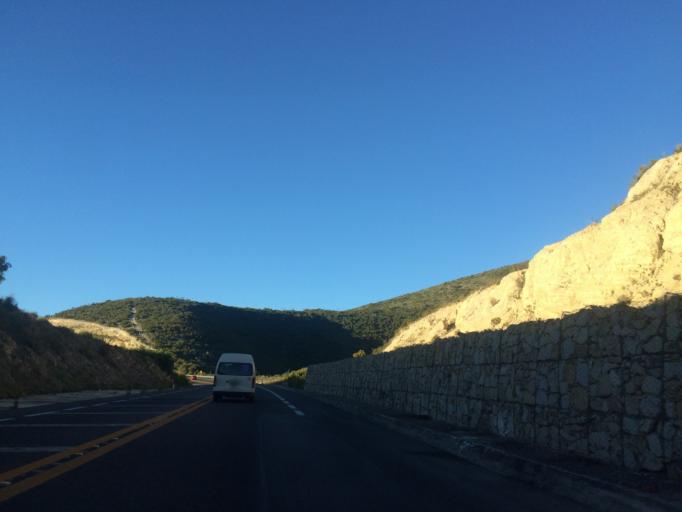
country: MX
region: Puebla
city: Chapuco
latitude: 18.6610
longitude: -97.4567
